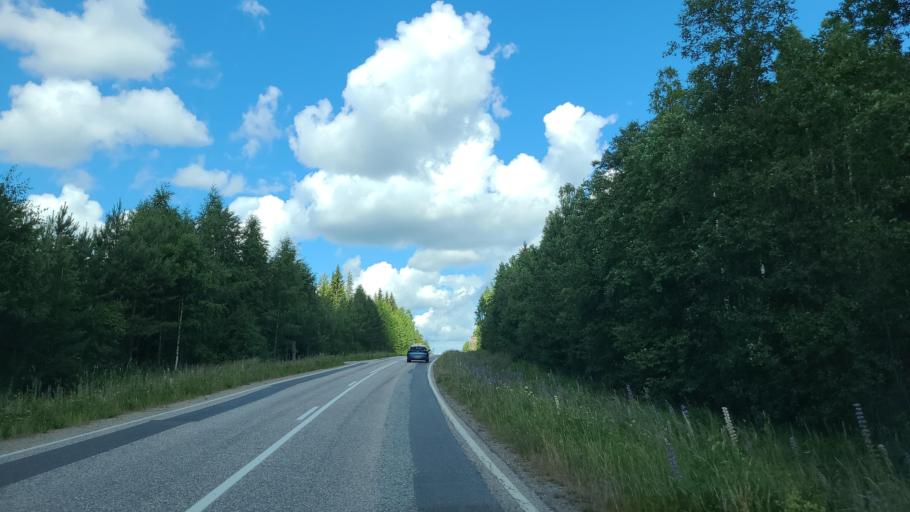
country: FI
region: Northern Savo
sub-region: Koillis-Savo
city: Kaavi
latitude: 62.9137
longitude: 28.7049
